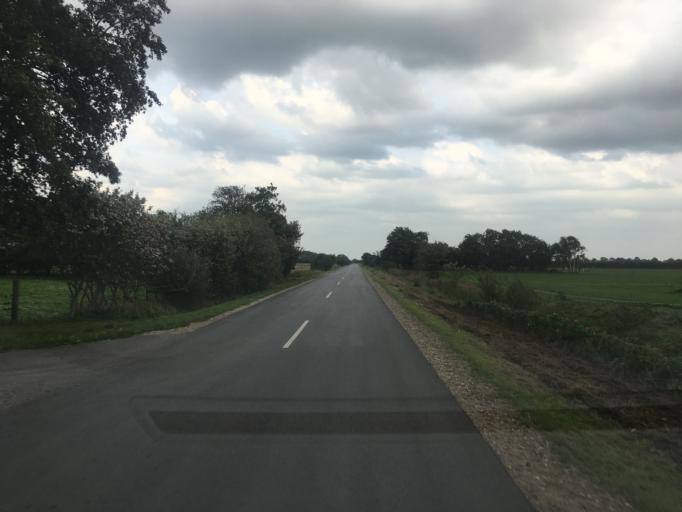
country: DK
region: South Denmark
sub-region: Tonder Kommune
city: Logumkloster
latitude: 55.0620
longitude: 9.0384
